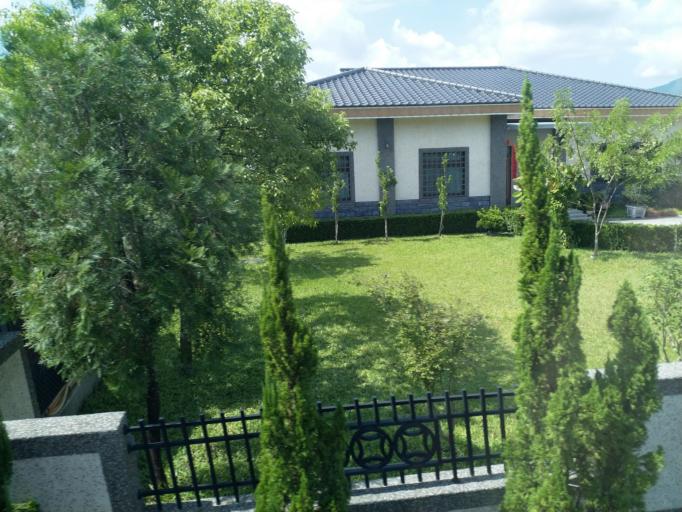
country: TW
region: Taiwan
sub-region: Pingtung
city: Pingtung
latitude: 22.8896
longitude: 120.5797
